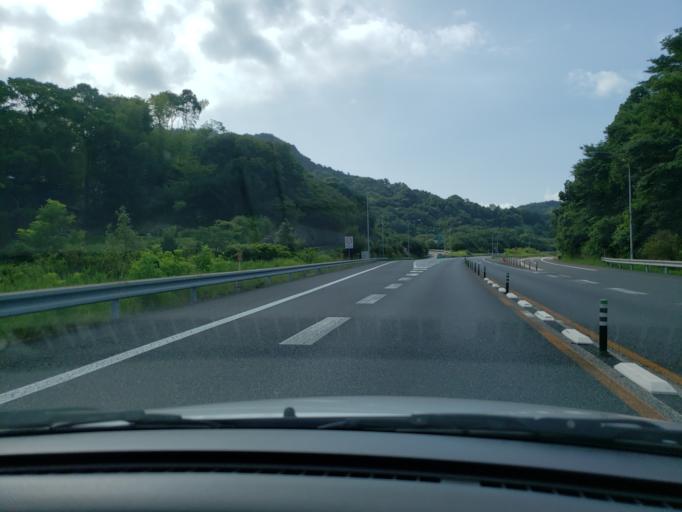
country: JP
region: Hiroshima
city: Innoshima
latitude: 34.2078
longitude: 133.0765
